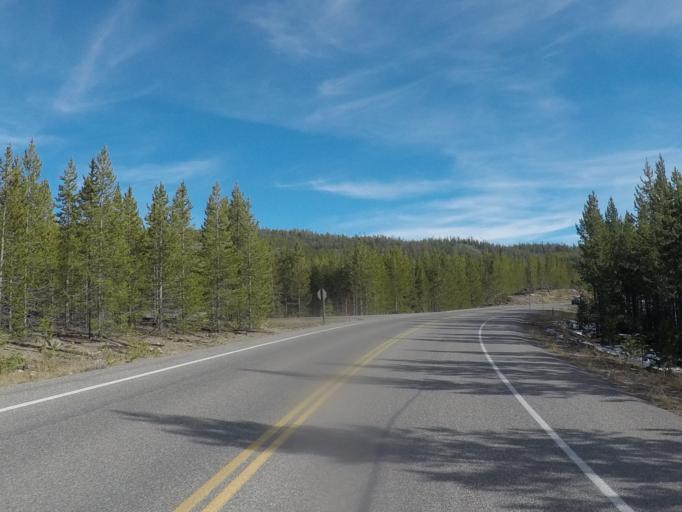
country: US
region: Montana
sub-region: Gallatin County
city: West Yellowstone
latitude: 44.6598
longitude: -110.7514
